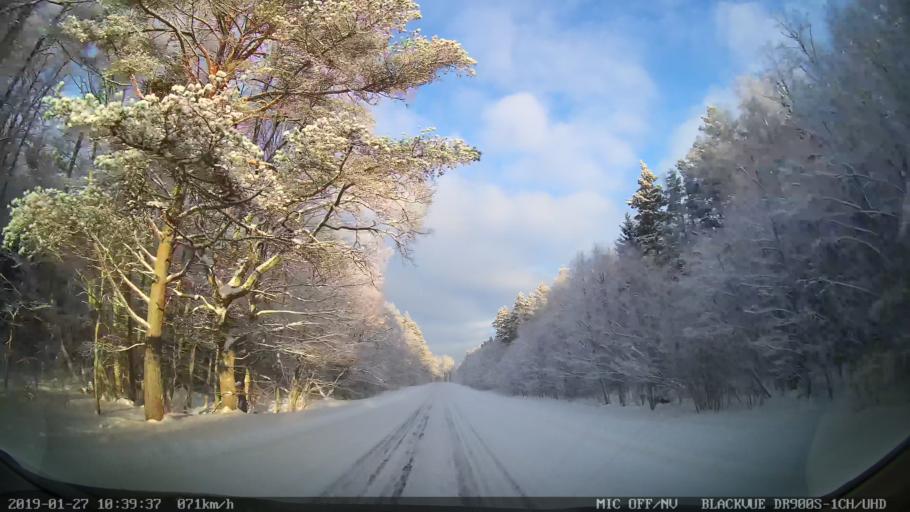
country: EE
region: Harju
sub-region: Raasiku vald
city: Raasiku
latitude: 59.4938
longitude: 25.2621
